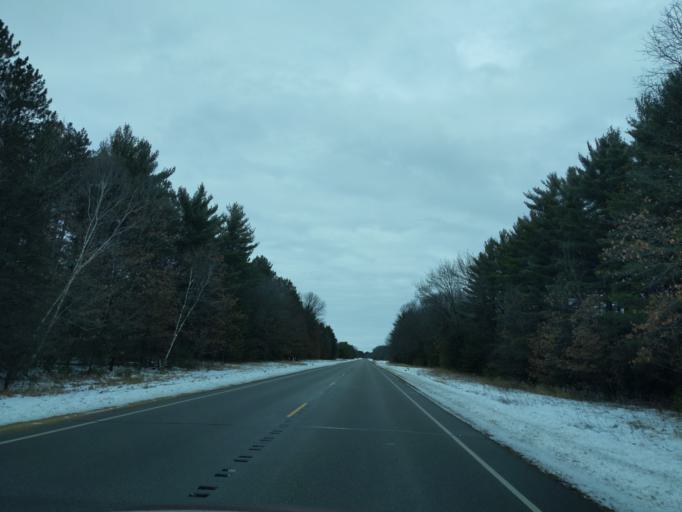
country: US
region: Wisconsin
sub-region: Marquette County
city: Montello
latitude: 43.9235
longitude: -89.3122
